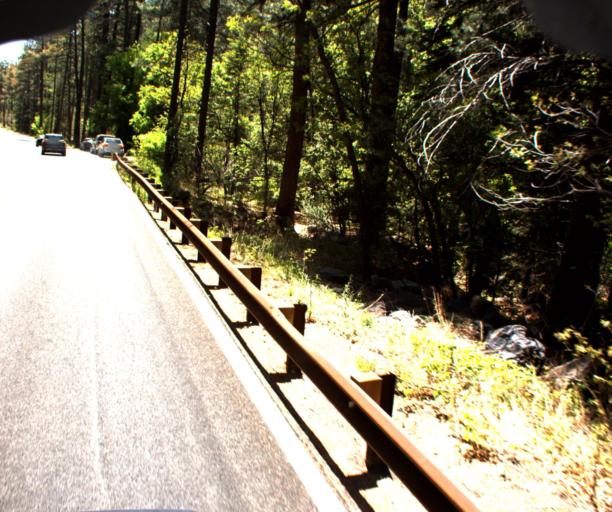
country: US
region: Arizona
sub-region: Coconino County
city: Kachina Village
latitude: 35.0150
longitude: -111.7376
